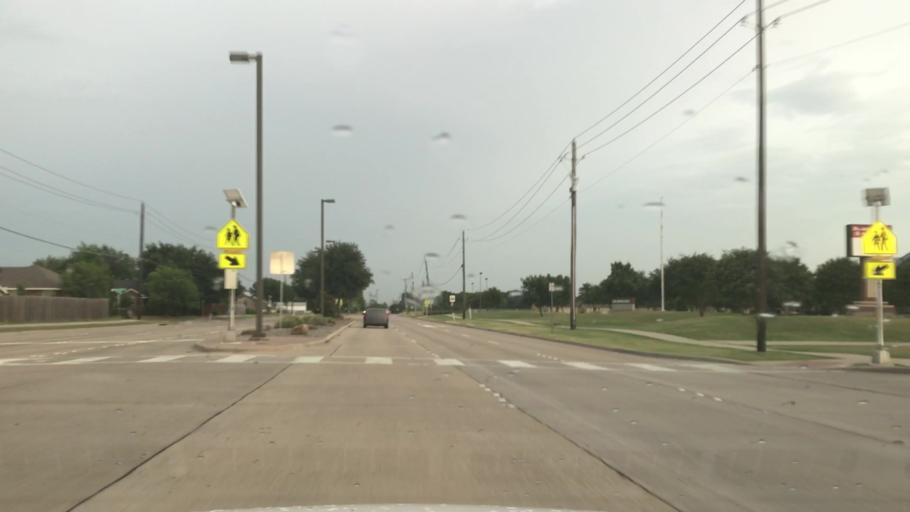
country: US
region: Texas
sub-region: Dallas County
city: Mesquite
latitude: 32.7331
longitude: -96.5570
